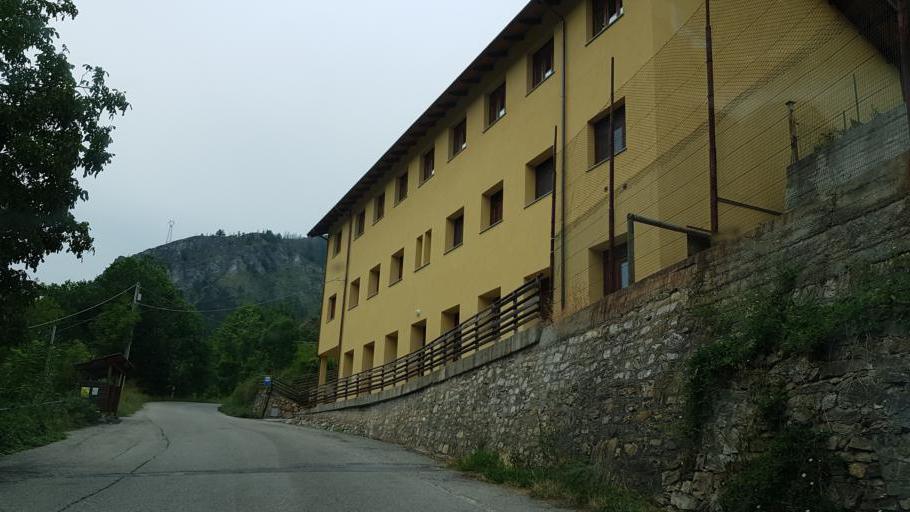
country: IT
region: Piedmont
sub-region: Provincia di Cuneo
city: Stroppo
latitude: 44.5041
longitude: 7.1305
